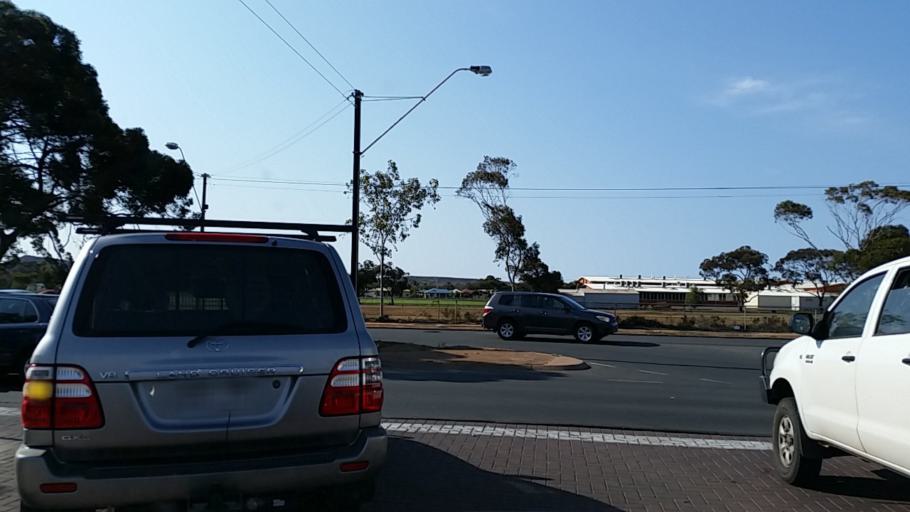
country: AU
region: South Australia
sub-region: Whyalla
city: Whyalla
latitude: -33.0280
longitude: 137.5396
